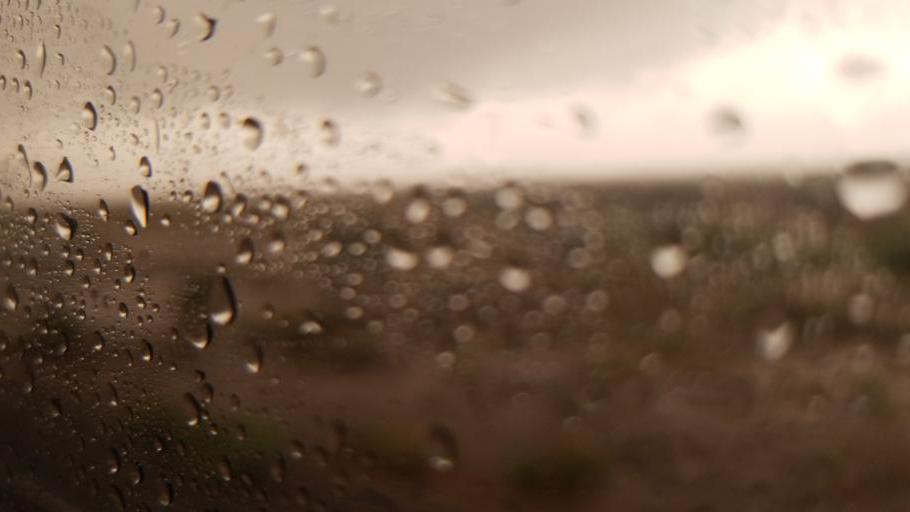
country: US
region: Arizona
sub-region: Navajo County
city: Joseph City
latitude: 34.9340
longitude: -110.2989
